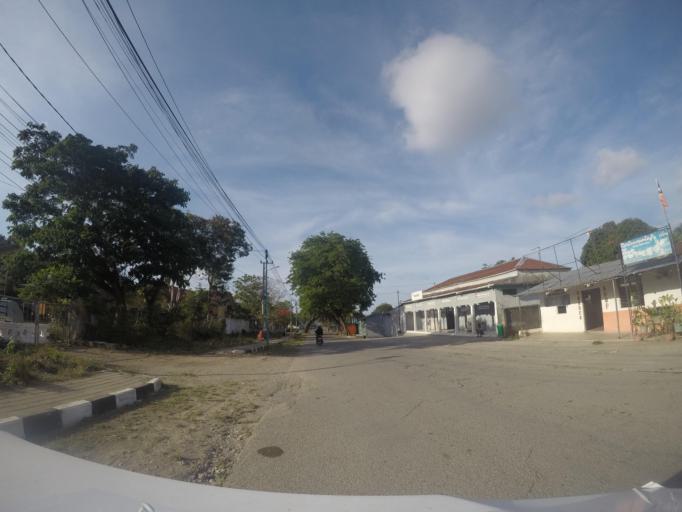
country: TL
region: Baucau
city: Baucau
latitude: -8.4749
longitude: 126.4583
